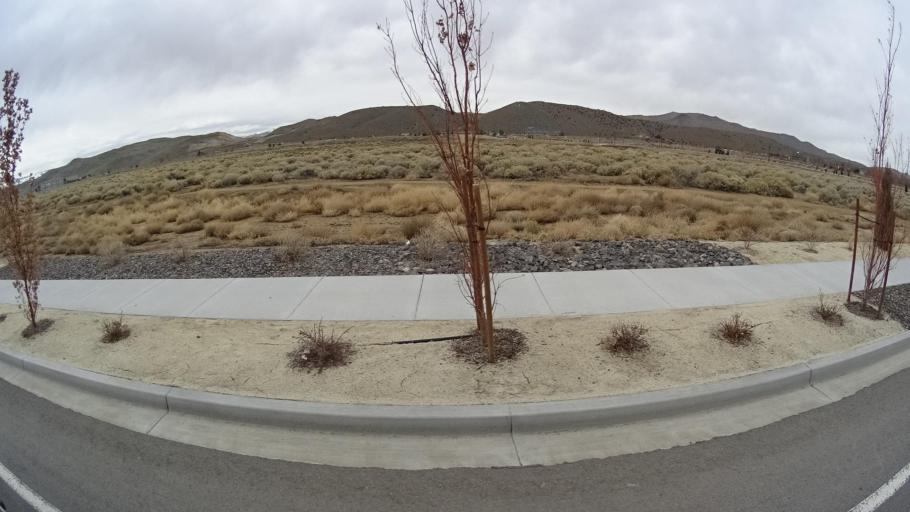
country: US
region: Nevada
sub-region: Washoe County
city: Spanish Springs
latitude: 39.6143
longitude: -119.7189
